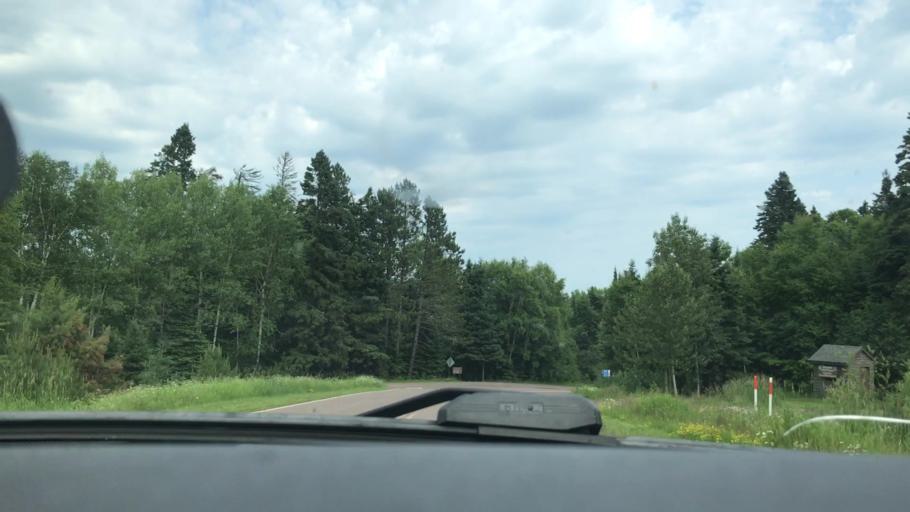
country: CA
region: Ontario
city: Neebing
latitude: 47.9646
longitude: -89.6865
